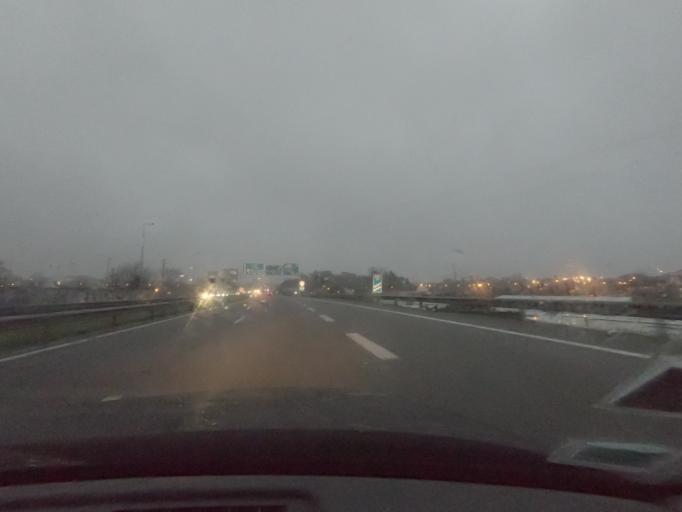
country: PT
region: Porto
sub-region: Matosinhos
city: Santa Cruz do Bispo
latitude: 41.2255
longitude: -8.6944
